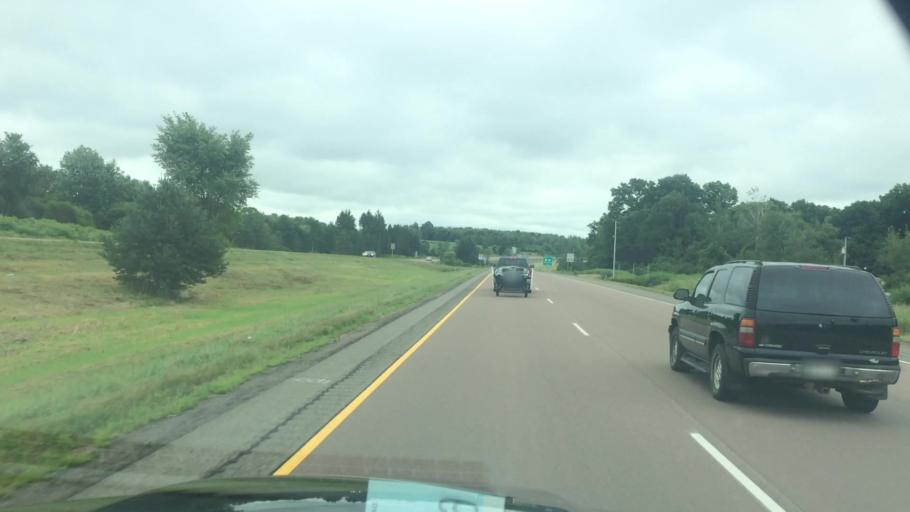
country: US
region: Wisconsin
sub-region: Marathon County
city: Wausau
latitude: 45.0126
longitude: -89.6653
